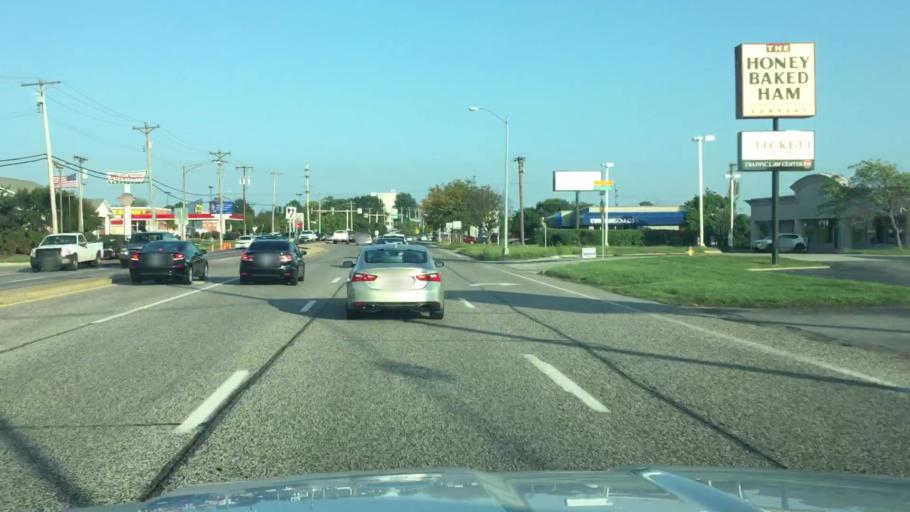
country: US
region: Missouri
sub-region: Saint Louis County
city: Mehlville
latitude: 38.5104
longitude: -90.3339
